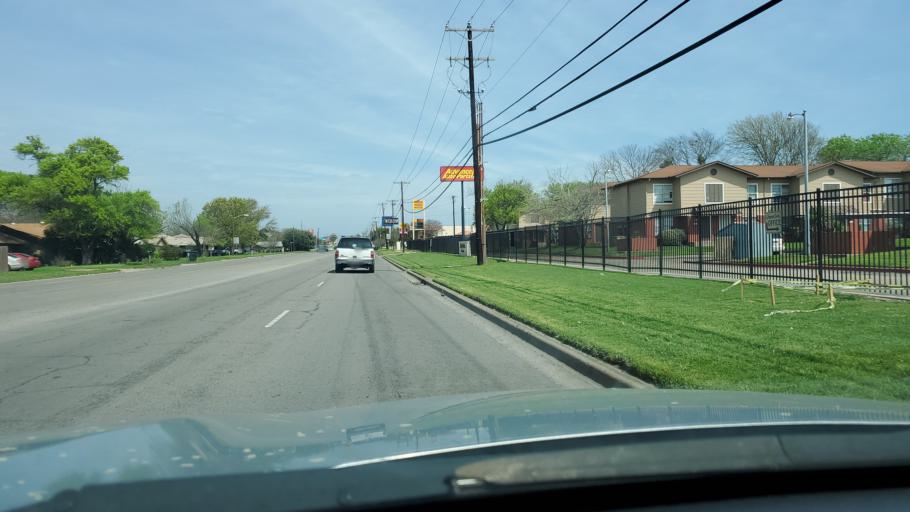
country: US
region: Texas
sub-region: Bell County
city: Temple
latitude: 31.0620
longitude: -97.3722
